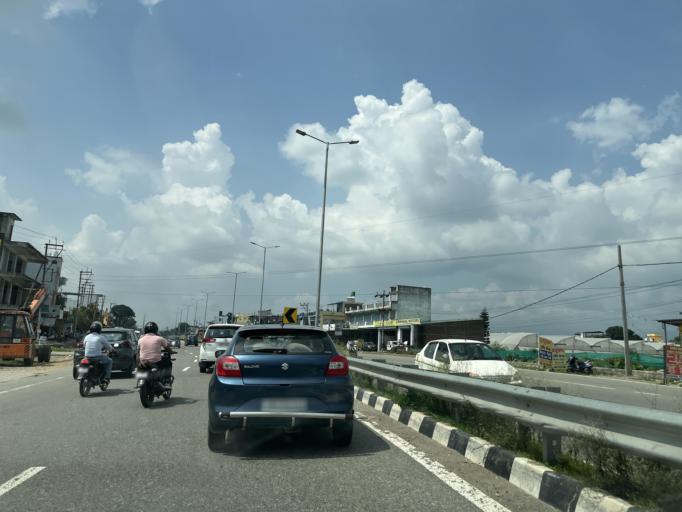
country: IN
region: Uttarakhand
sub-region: Dehradun
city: Raipur
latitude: 30.2545
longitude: 78.0935
